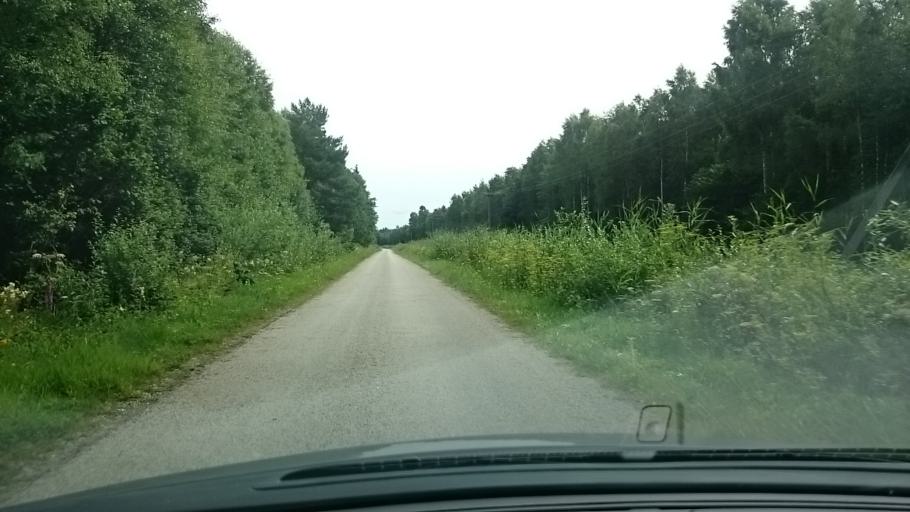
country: EE
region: Laeaene
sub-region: Haapsalu linn
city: Haapsalu
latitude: 59.0101
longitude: 23.5377
